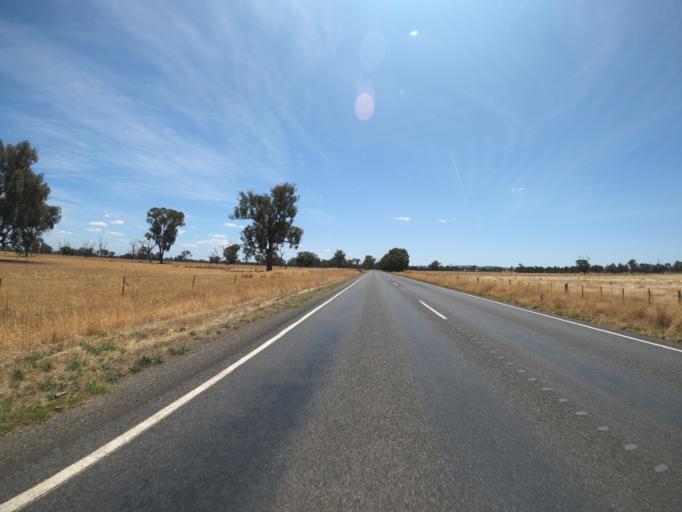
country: AU
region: Victoria
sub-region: Benalla
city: Benalla
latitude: -36.5113
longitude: 146.0289
